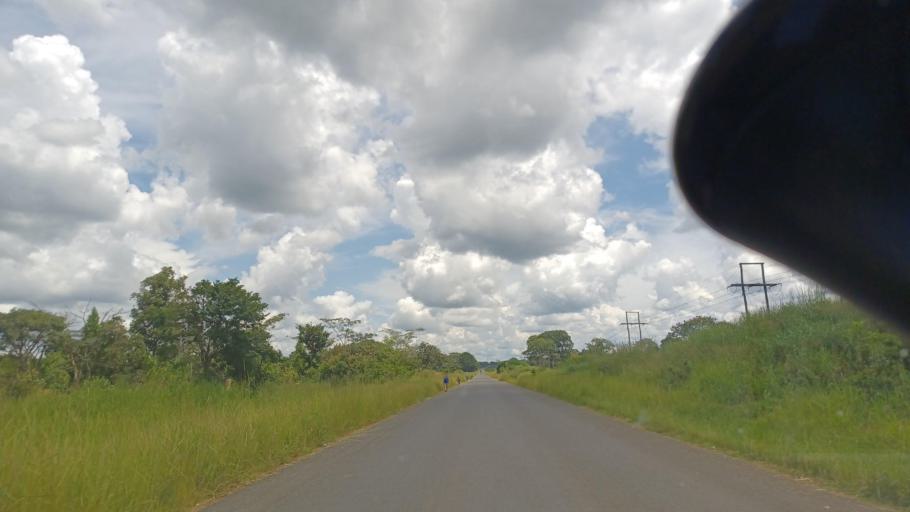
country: ZM
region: North-Western
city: Solwezi
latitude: -12.4221
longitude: 26.2225
